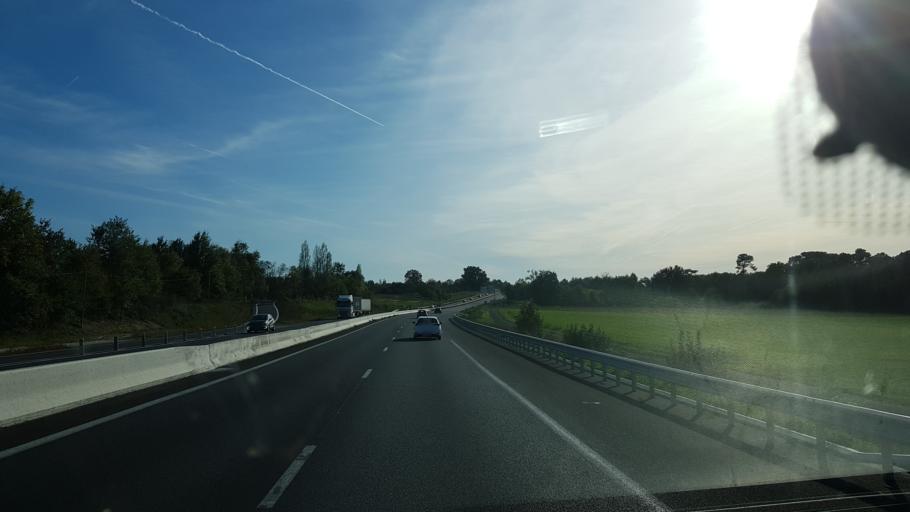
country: FR
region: Poitou-Charentes
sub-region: Departement de la Charente-Maritime
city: Chevanceaux
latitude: 45.3170
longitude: -0.2303
